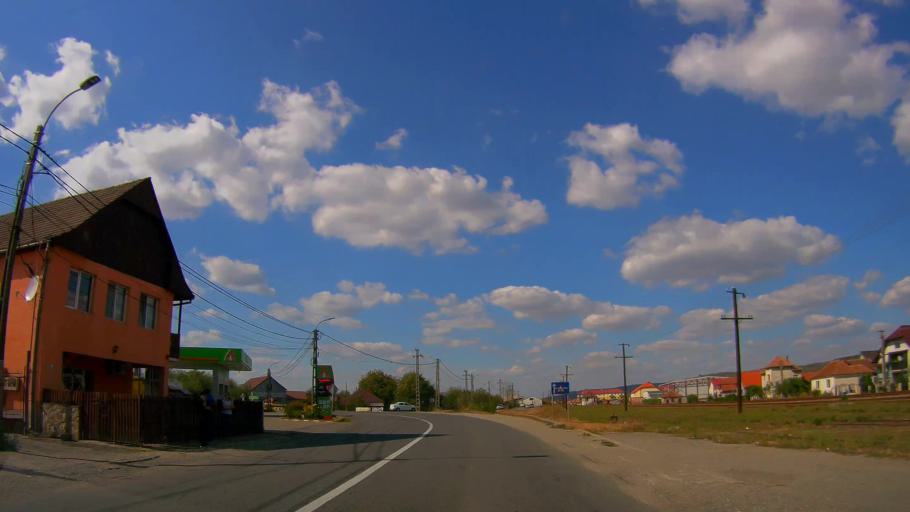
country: RO
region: Salaj
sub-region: Comuna Sarmasag
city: Sarmasag
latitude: 47.3464
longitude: 22.8240
